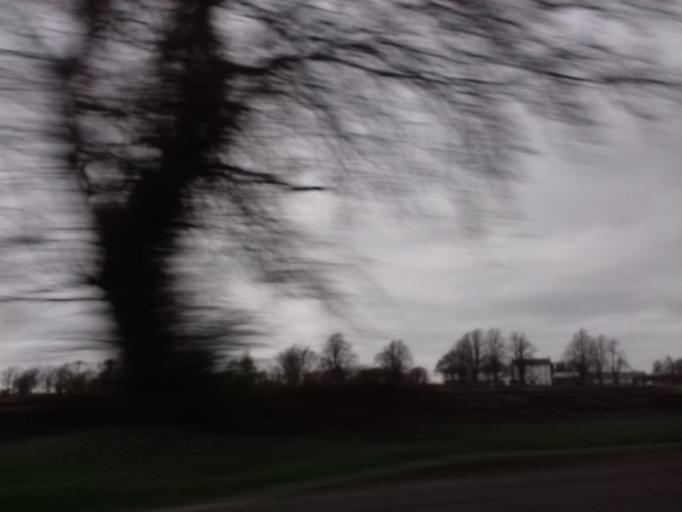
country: IE
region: Munster
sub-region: County Limerick
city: Adare
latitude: 52.5396
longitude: -8.8600
